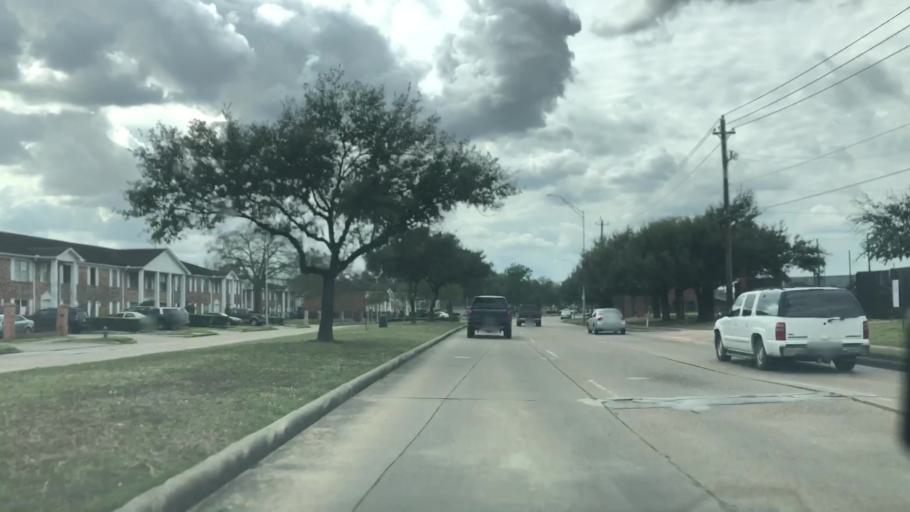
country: US
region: Texas
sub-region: Harris County
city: Bellaire
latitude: 29.6917
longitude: -95.5116
